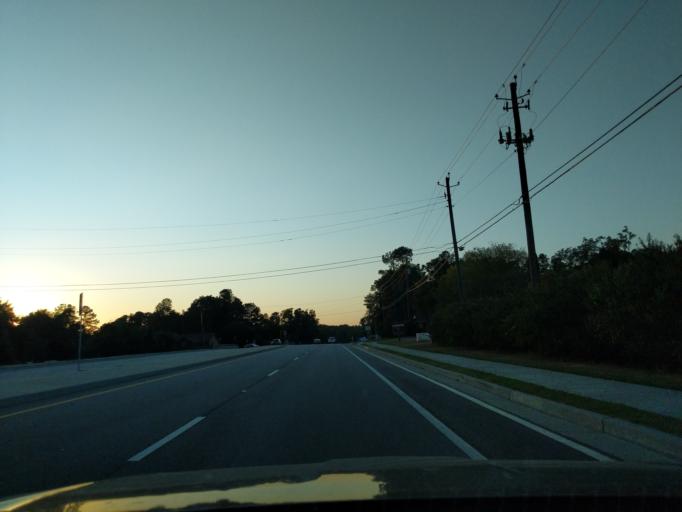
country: US
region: Georgia
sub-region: Columbia County
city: Martinez
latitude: 33.5210
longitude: -82.0854
